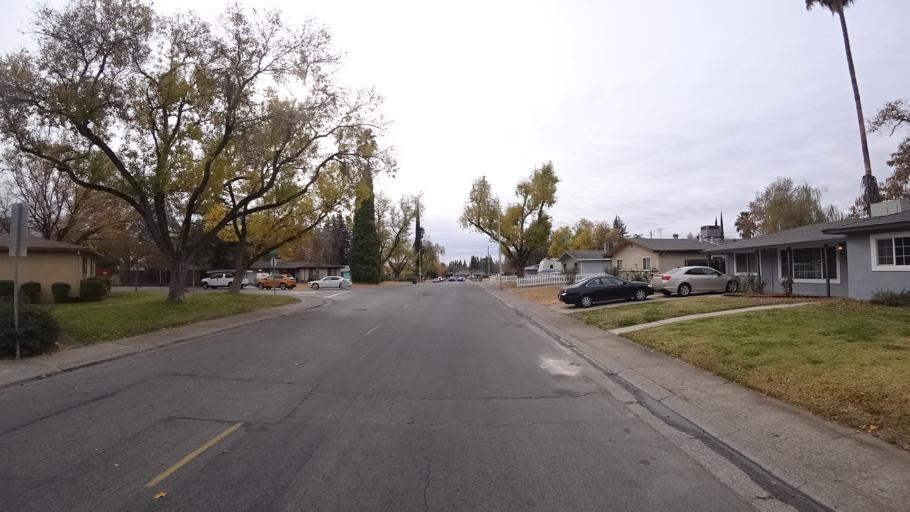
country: US
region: California
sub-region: Sacramento County
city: Citrus Heights
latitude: 38.7092
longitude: -121.3005
